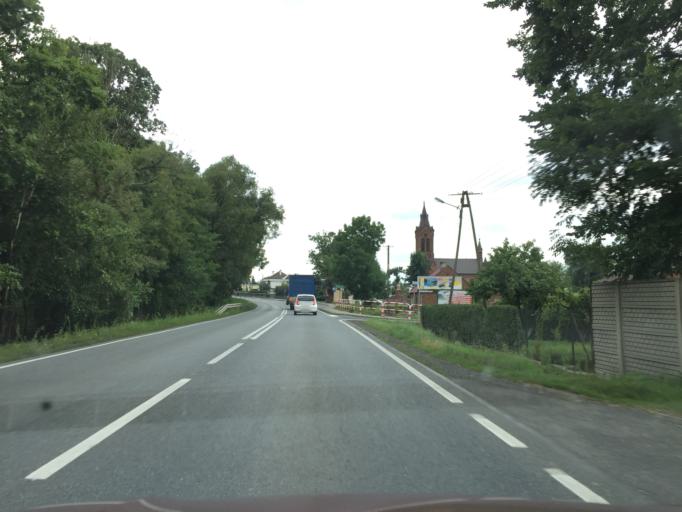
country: PL
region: Greater Poland Voivodeship
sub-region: Kalisz
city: Kalisz
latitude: 51.8148
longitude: 18.0928
